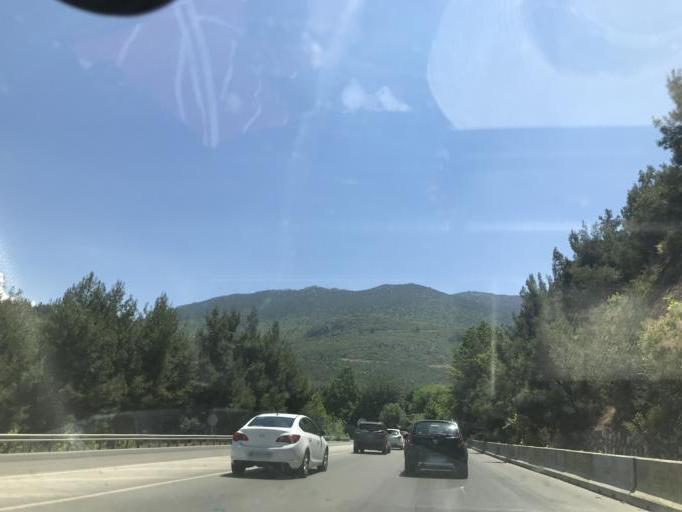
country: TR
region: Denizli
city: Denizli
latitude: 37.7294
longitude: 29.1654
